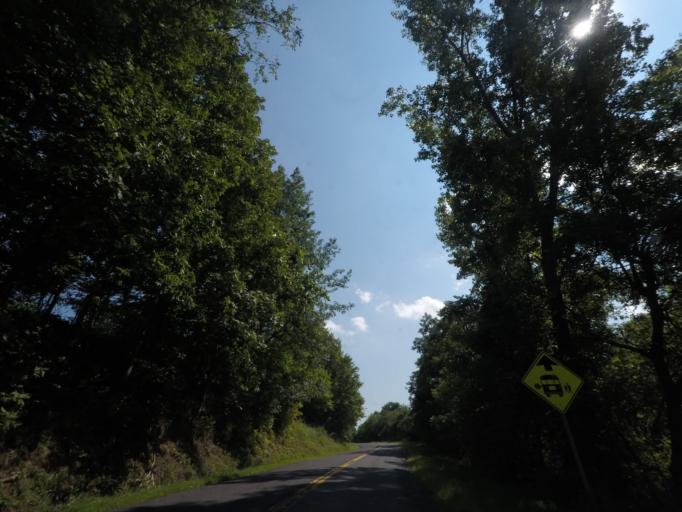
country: US
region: New York
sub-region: Saratoga County
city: Waterford
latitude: 42.8104
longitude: -73.5927
